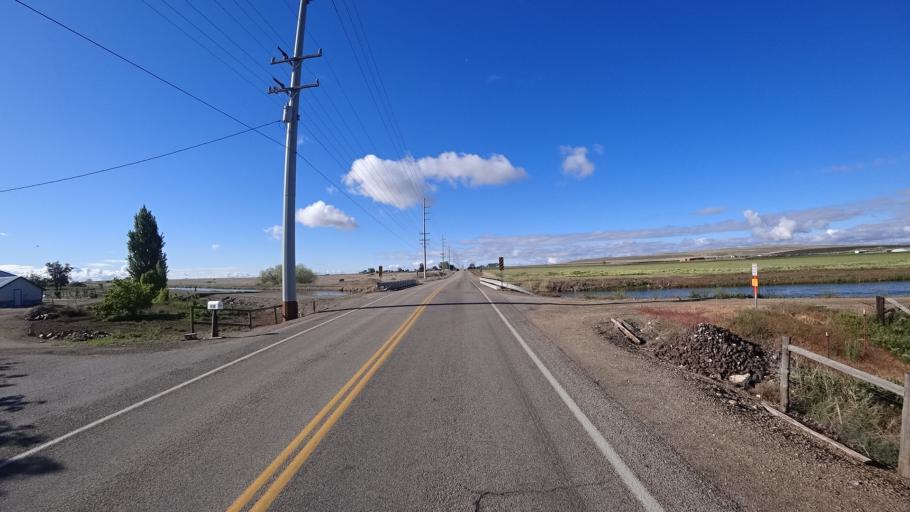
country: US
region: Idaho
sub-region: Ada County
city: Kuna
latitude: 43.4714
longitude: -116.4137
